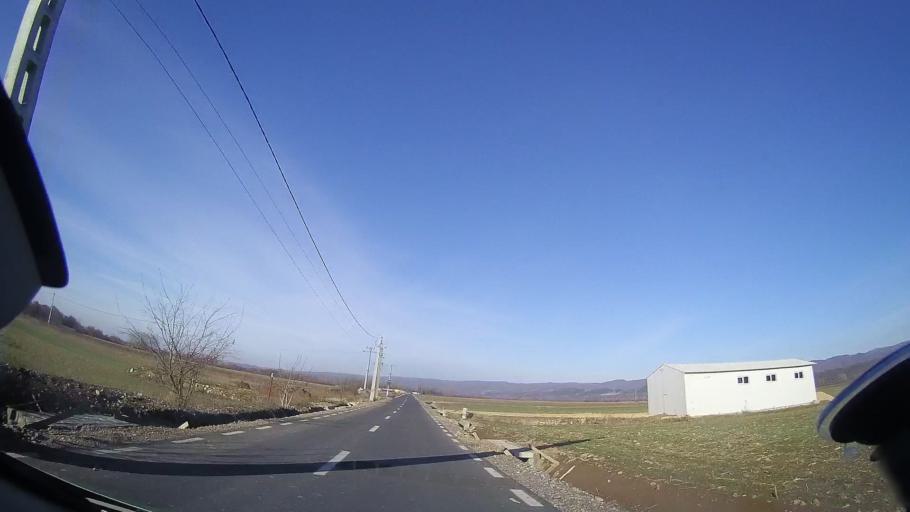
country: RO
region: Bihor
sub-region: Comuna Vadu Crisului
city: Vadu Crisului
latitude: 46.9939
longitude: 22.5077
